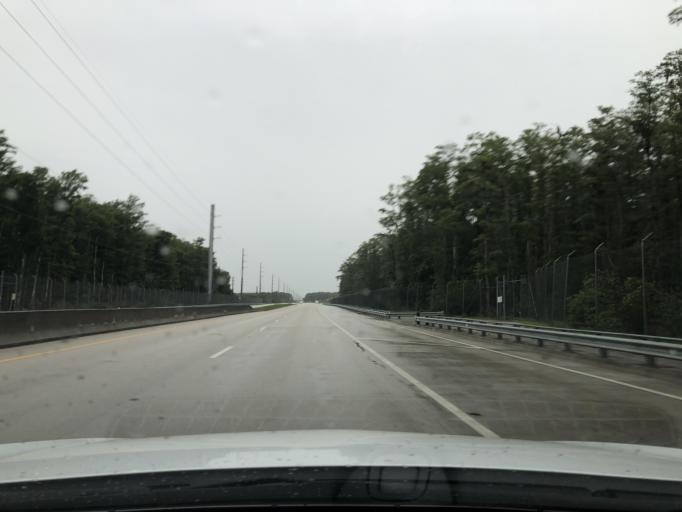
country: US
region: Florida
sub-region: Collier County
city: Orangetree
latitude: 26.2940
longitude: -81.4787
